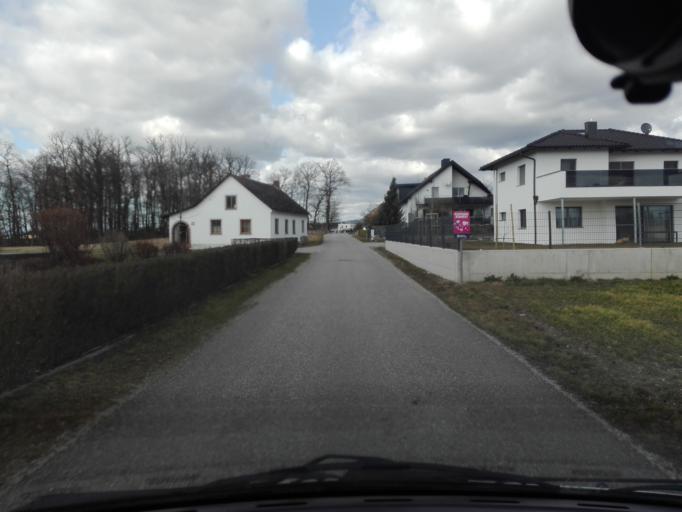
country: AT
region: Lower Austria
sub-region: Politischer Bezirk Amstetten
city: Strengberg
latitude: 48.1912
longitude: 14.6835
